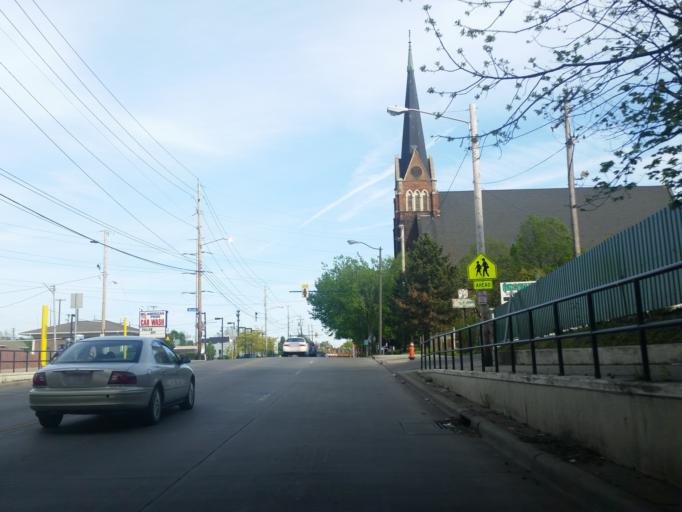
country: US
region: Ohio
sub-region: Cuyahoga County
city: Newburgh Heights
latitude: 41.4508
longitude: -81.6302
